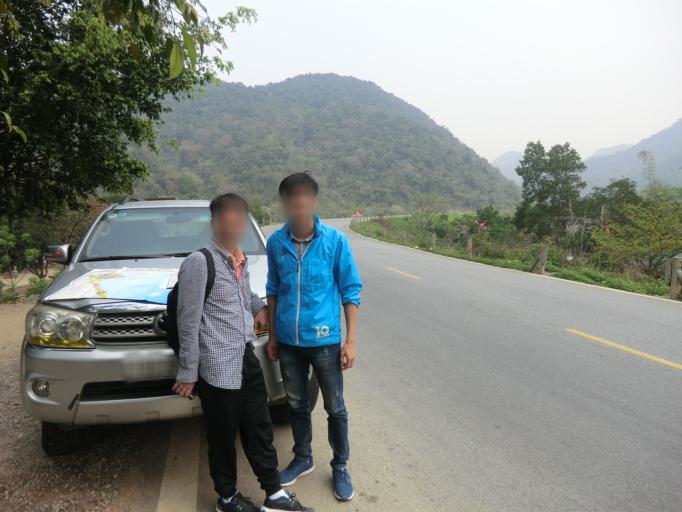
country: VN
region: Hoa Binh
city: Thi Tran Hang Tram
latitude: 20.3517
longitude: 105.5236
